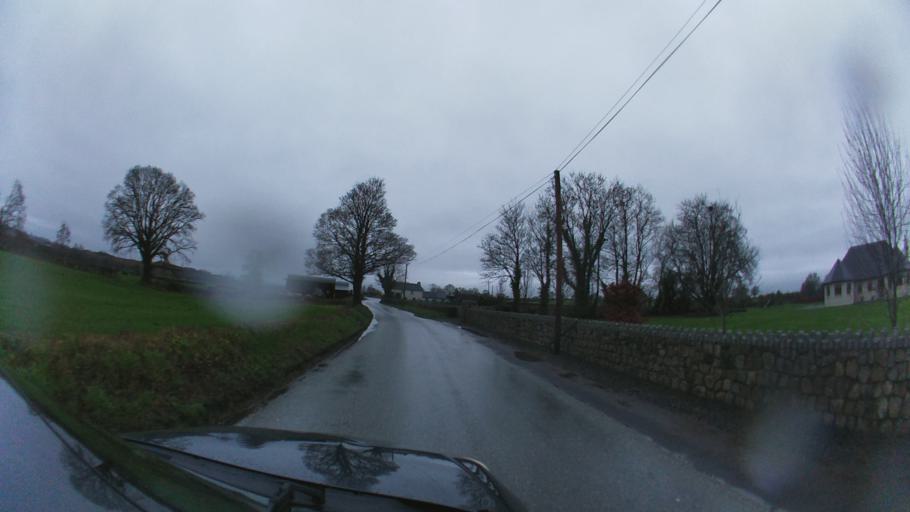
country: IE
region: Leinster
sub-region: County Carlow
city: Bagenalstown
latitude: 52.6465
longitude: -6.9892
